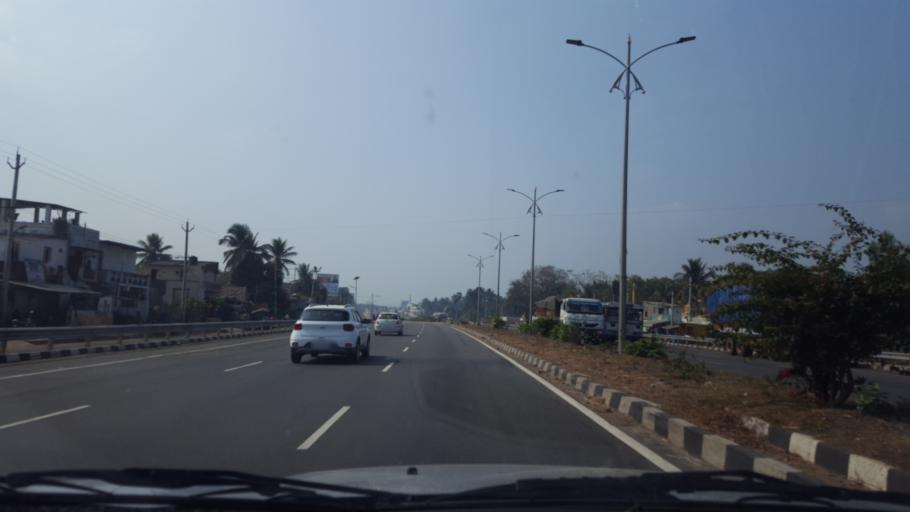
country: IN
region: Andhra Pradesh
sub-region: Vishakhapatnam
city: Bhimunipatnam
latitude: 17.9177
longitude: 83.4155
